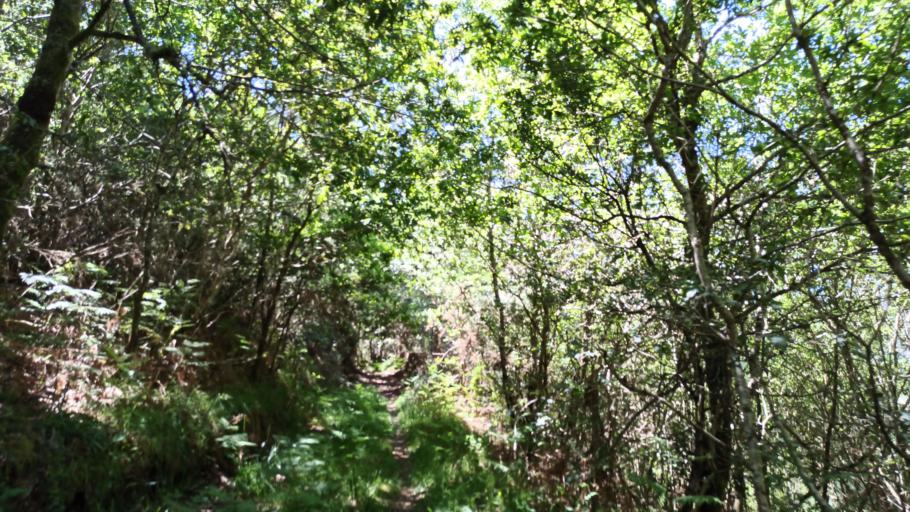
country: ES
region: Galicia
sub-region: Provincia da Coruna
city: Negreira
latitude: 42.9219
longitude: -8.7193
